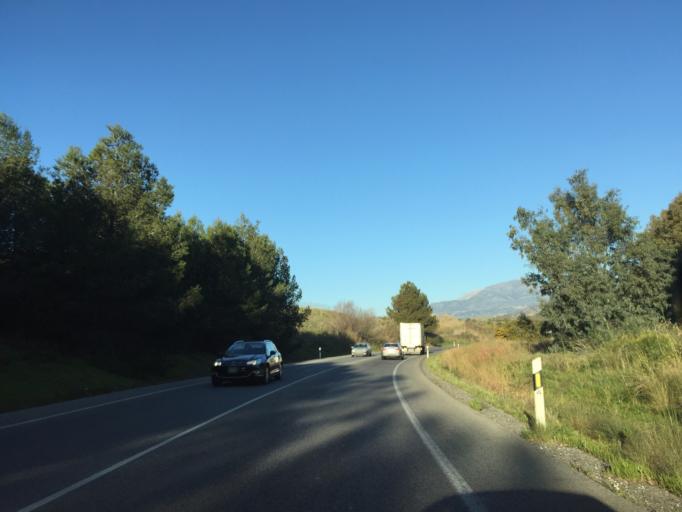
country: ES
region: Andalusia
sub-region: Provincia de Malaga
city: Pizarra
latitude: 36.7198
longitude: -4.7045
